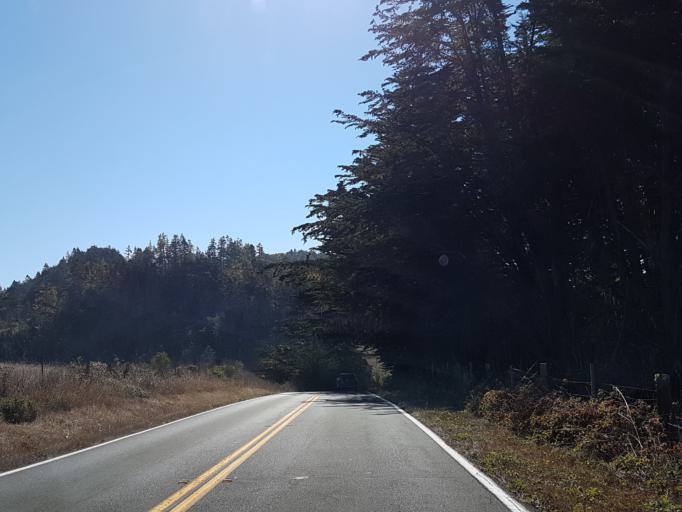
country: US
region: California
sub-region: Mendocino County
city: Boonville
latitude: 39.0526
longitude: -123.6845
